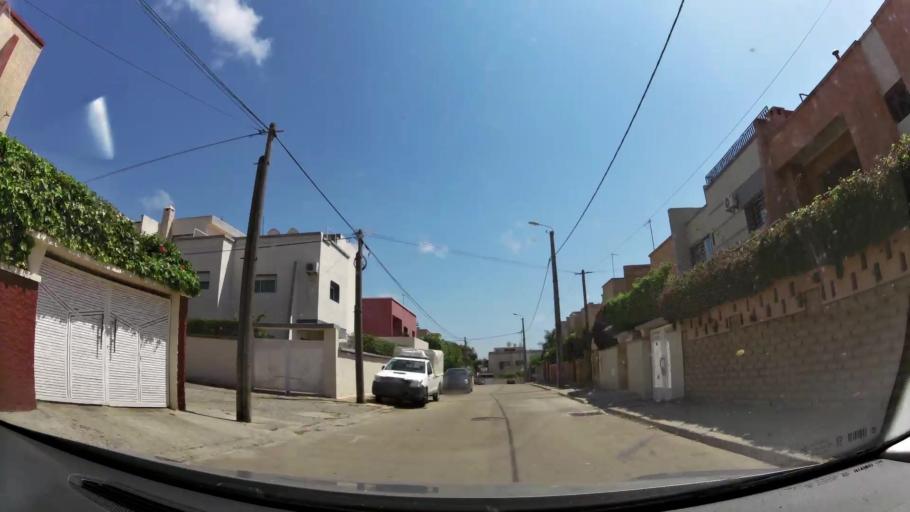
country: MA
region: Rabat-Sale-Zemmour-Zaer
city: Sale
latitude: 34.0440
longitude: -6.7863
